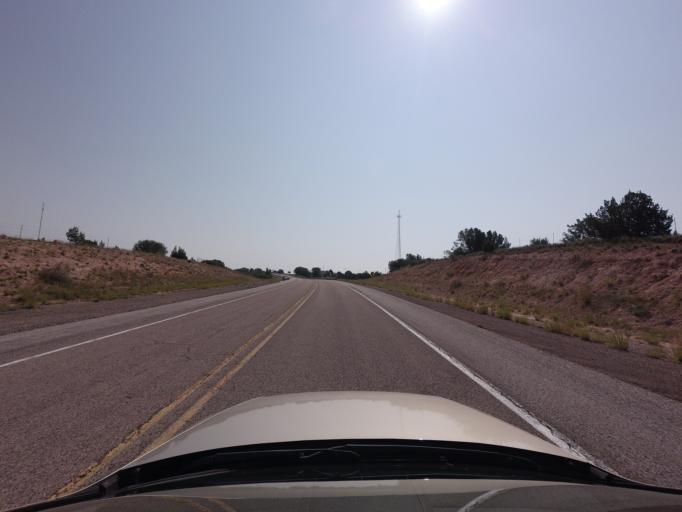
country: US
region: New Mexico
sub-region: Quay County
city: Tucumcari
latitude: 34.8225
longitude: -103.7460
